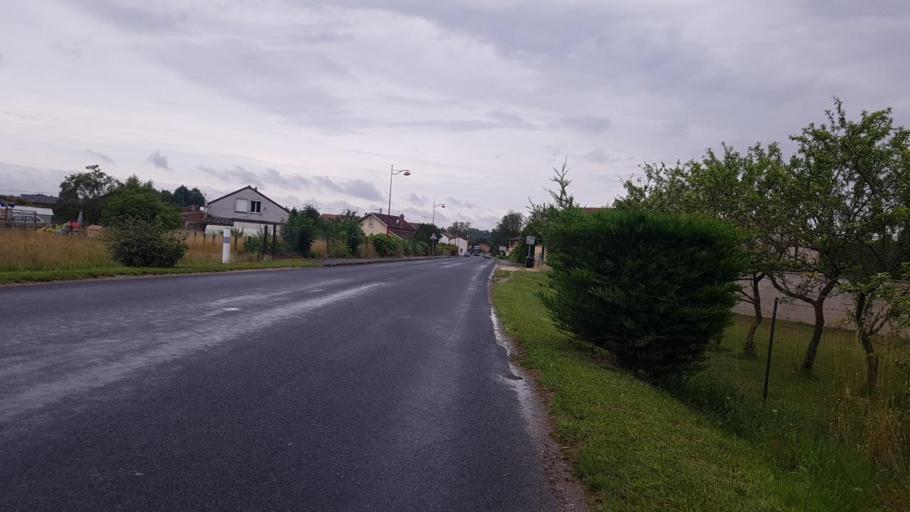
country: FR
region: Champagne-Ardenne
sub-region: Departement de la Marne
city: Vitry-le-Francois
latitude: 48.7405
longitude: 4.6378
